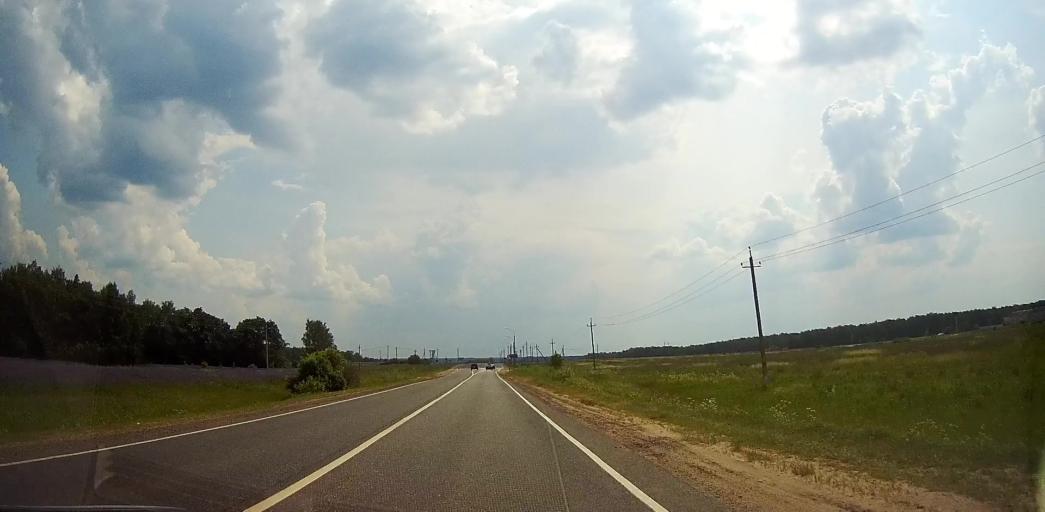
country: RU
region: Moskovskaya
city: Stupino
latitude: 54.9591
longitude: 38.1236
